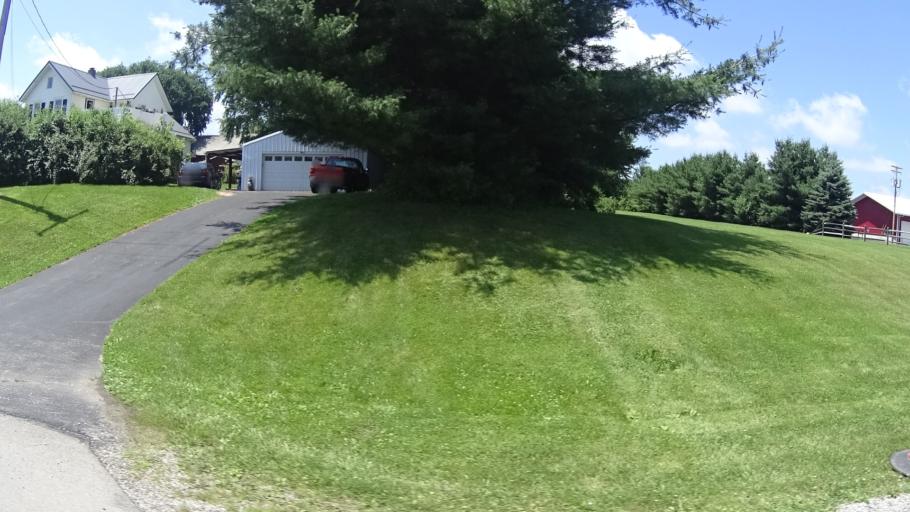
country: US
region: Ohio
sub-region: Huron County
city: Wakeman
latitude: 41.3324
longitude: -82.3605
